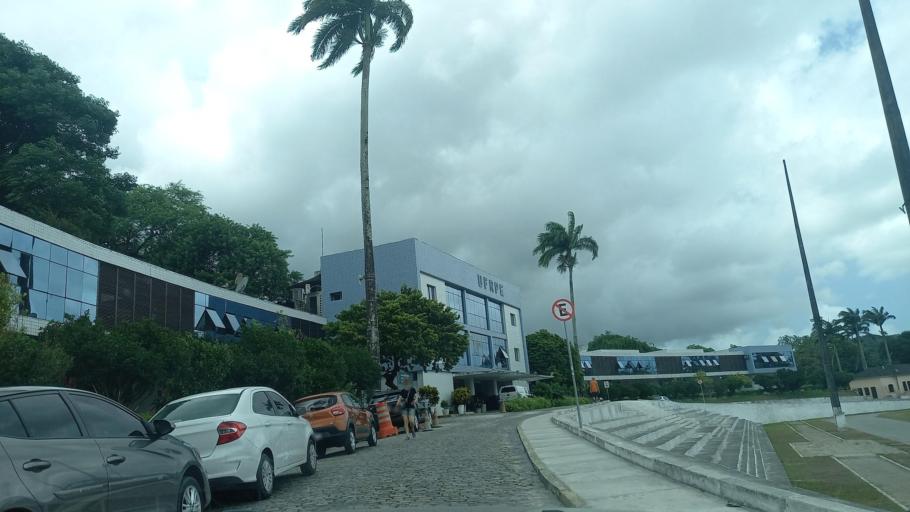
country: BR
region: Pernambuco
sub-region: Sao Lourenco Da Mata
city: Sao Lourenco da Mata
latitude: -8.0150
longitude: -34.9506
